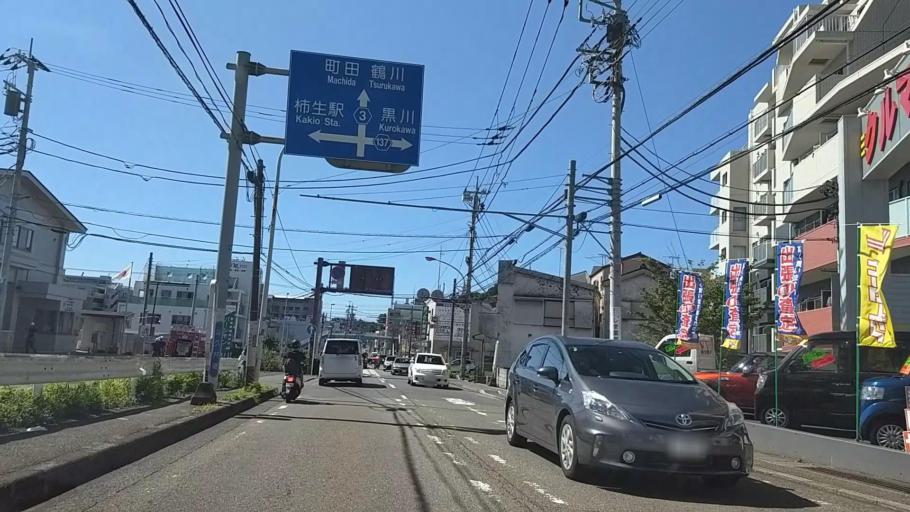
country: JP
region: Tokyo
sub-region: Machida-shi
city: Machida
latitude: 35.5919
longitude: 139.4975
